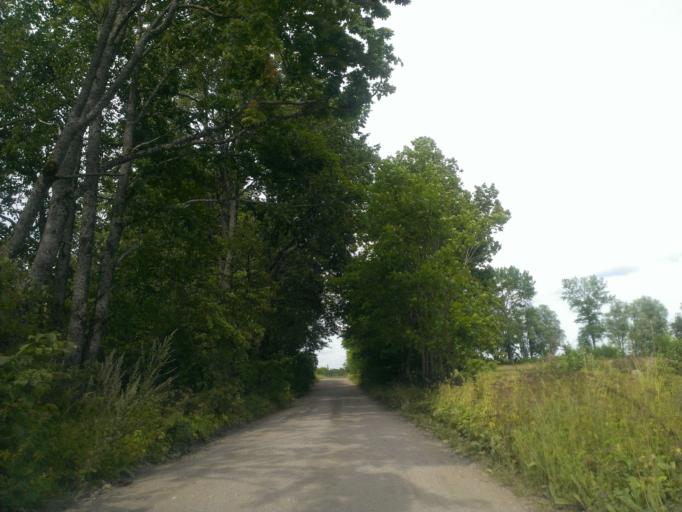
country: LV
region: Ligatne
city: Ligatne
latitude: 57.2174
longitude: 25.0287
